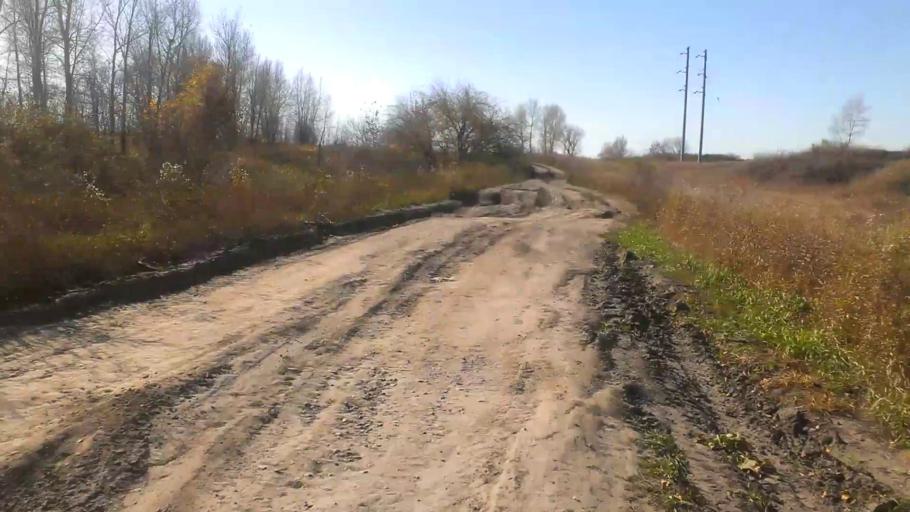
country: RU
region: Altai Krai
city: Novoaltaysk
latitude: 53.3682
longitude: 83.9477
